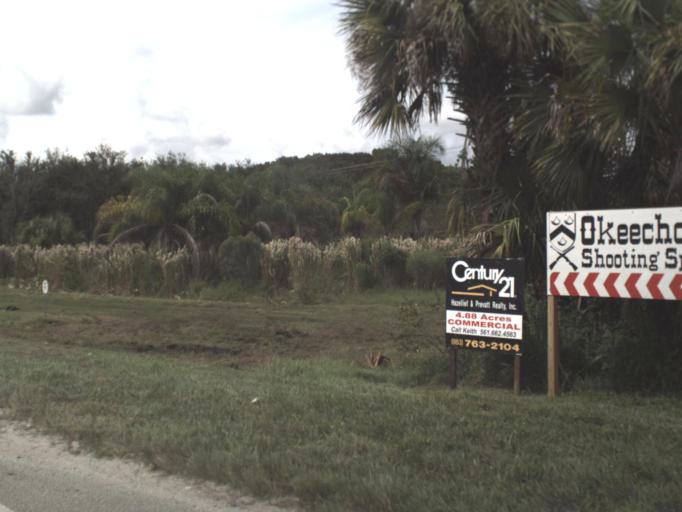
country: US
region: Florida
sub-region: Okeechobee County
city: Taylor Creek
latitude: 27.2911
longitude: -80.6973
